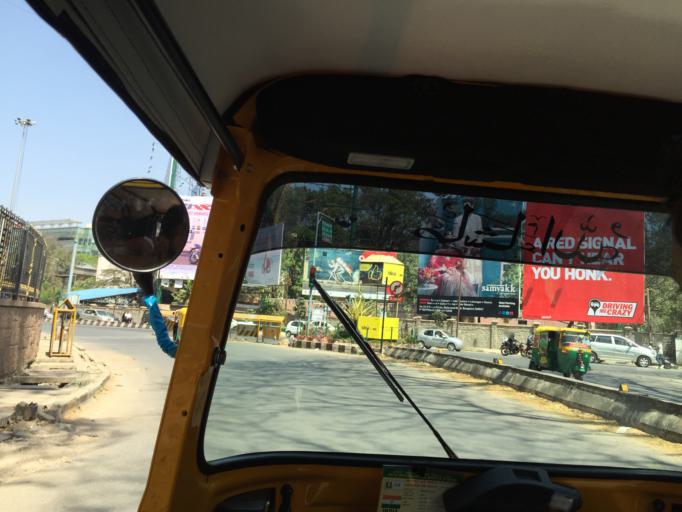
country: IN
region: Karnataka
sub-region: Bangalore Urban
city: Bangalore
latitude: 12.9714
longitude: 77.6192
